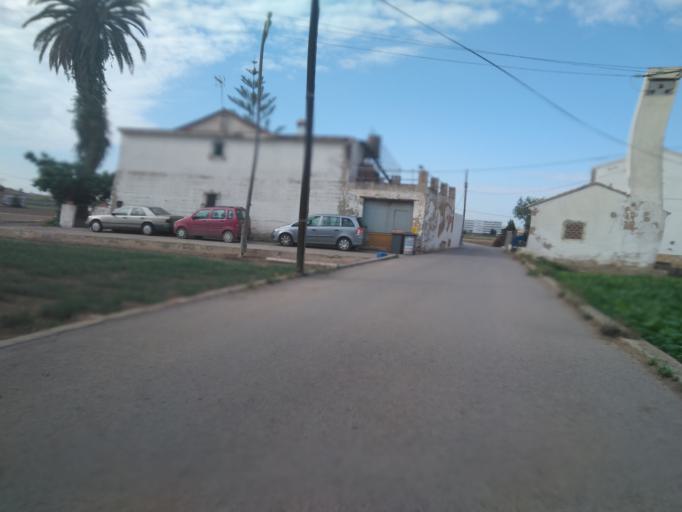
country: ES
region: Valencia
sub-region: Provincia de Valencia
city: Alboraya
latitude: 39.4928
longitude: -0.3400
